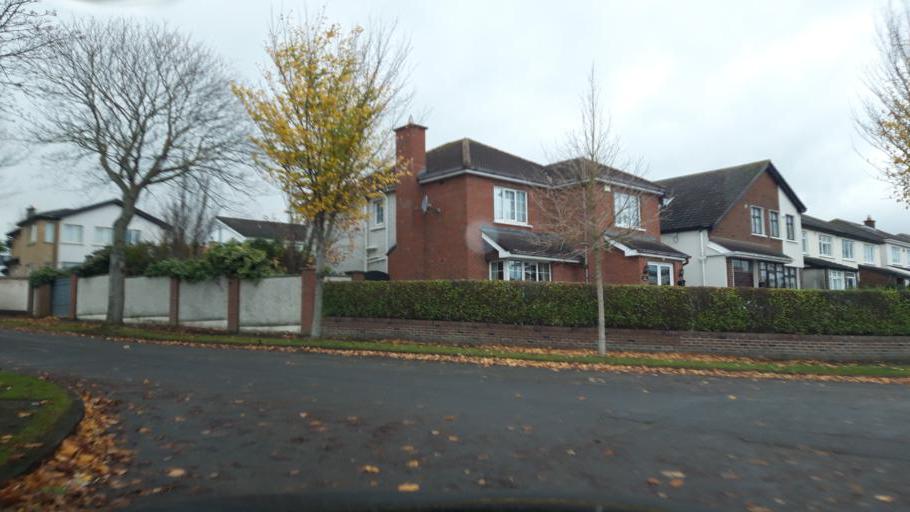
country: IE
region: Leinster
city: Malahide
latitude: 53.4471
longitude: -6.1382
